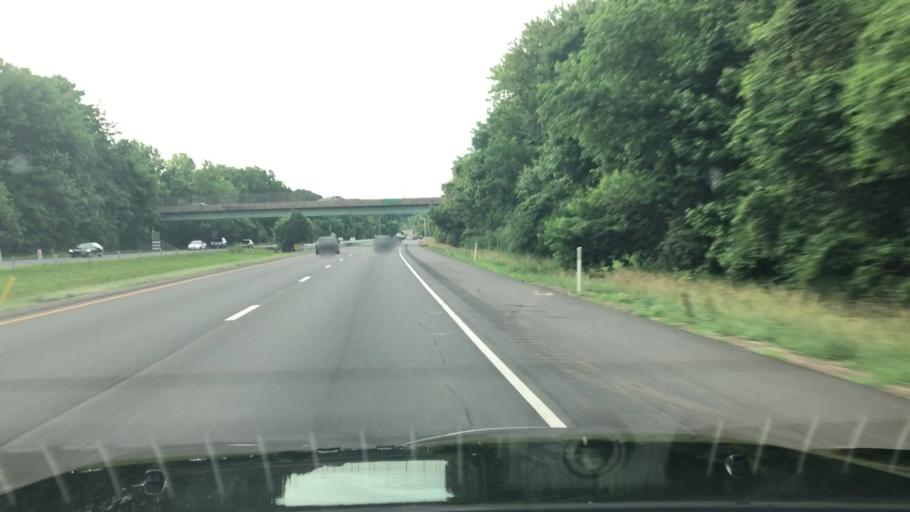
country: US
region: Pennsylvania
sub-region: Bucks County
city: Hulmeville
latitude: 40.1563
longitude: -74.8998
